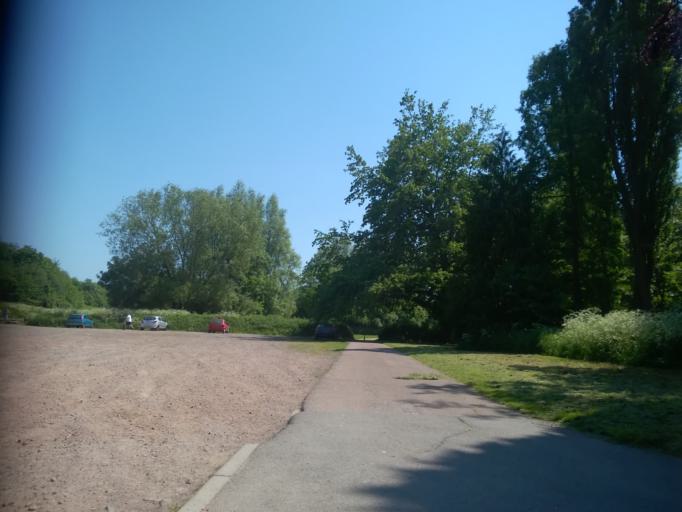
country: GB
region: England
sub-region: Leicestershire
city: Glenfield
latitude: 52.6222
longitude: -1.1794
